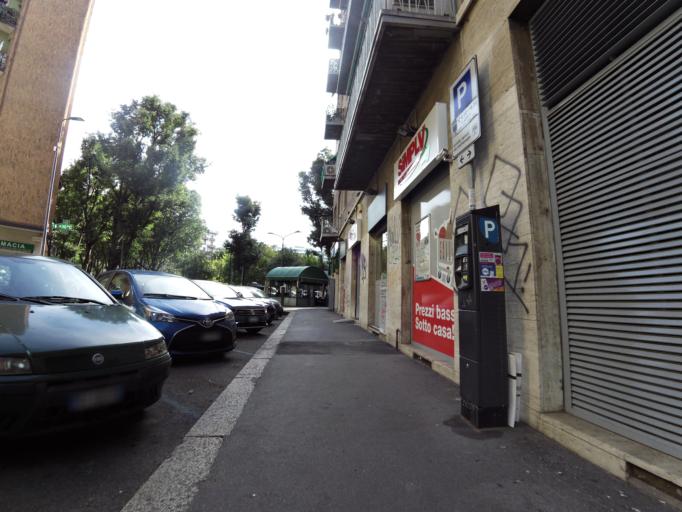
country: IT
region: Lombardy
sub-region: Citta metropolitana di Milano
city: Milano
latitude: 45.4781
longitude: 9.1618
